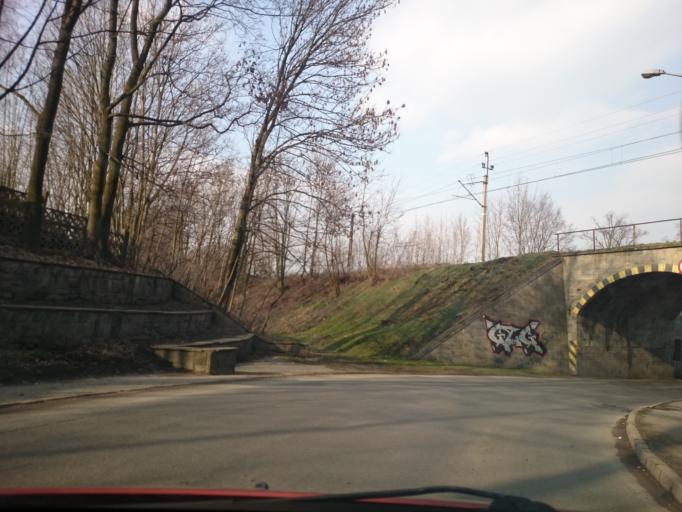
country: PL
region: Lower Silesian Voivodeship
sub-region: Powiat klodzki
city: Bystrzyca Klodzka
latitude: 50.3024
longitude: 16.6547
